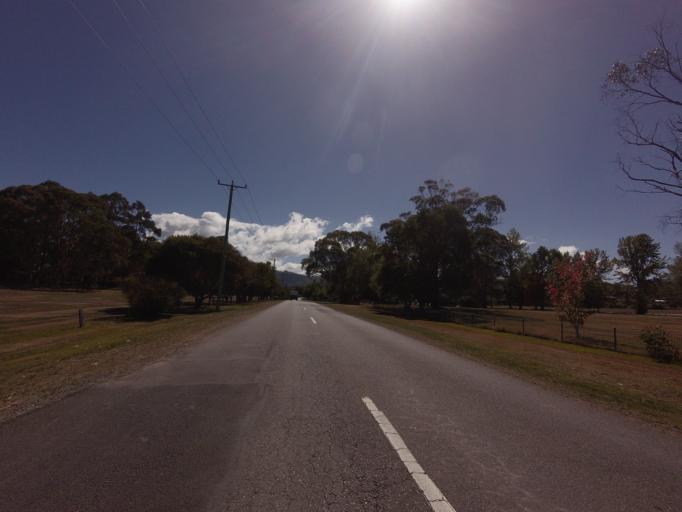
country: AU
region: Tasmania
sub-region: Break O'Day
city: St Helens
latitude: -41.5855
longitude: 148.1871
